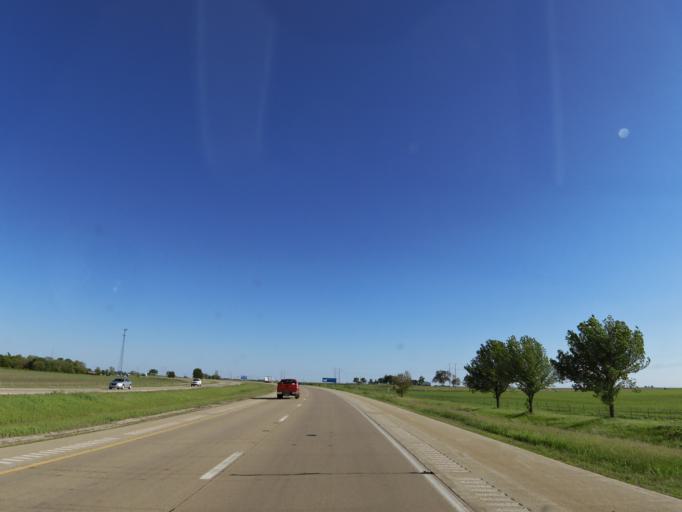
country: US
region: Illinois
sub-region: Marshall County
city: Wenona
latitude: 41.0557
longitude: -89.0669
